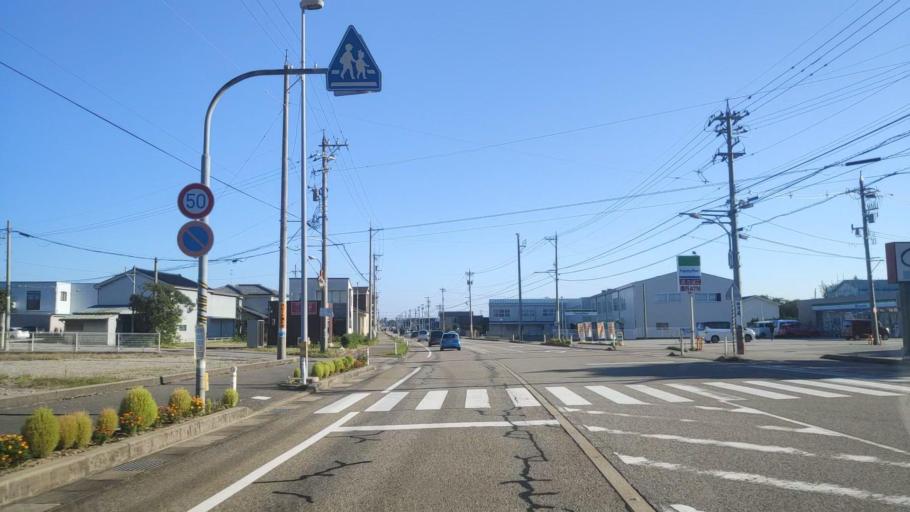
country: JP
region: Ishikawa
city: Tsubata
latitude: 36.7436
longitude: 136.7082
